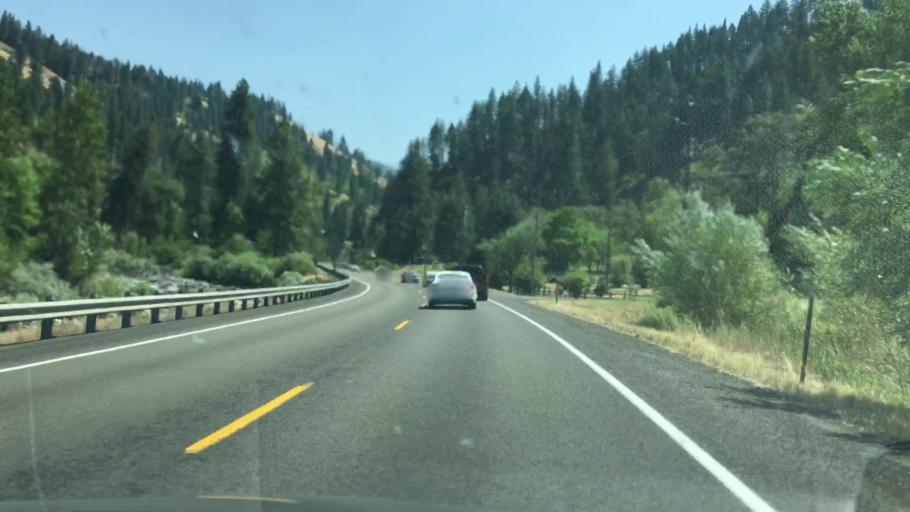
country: US
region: Idaho
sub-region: Valley County
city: McCall
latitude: 45.2392
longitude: -116.3308
